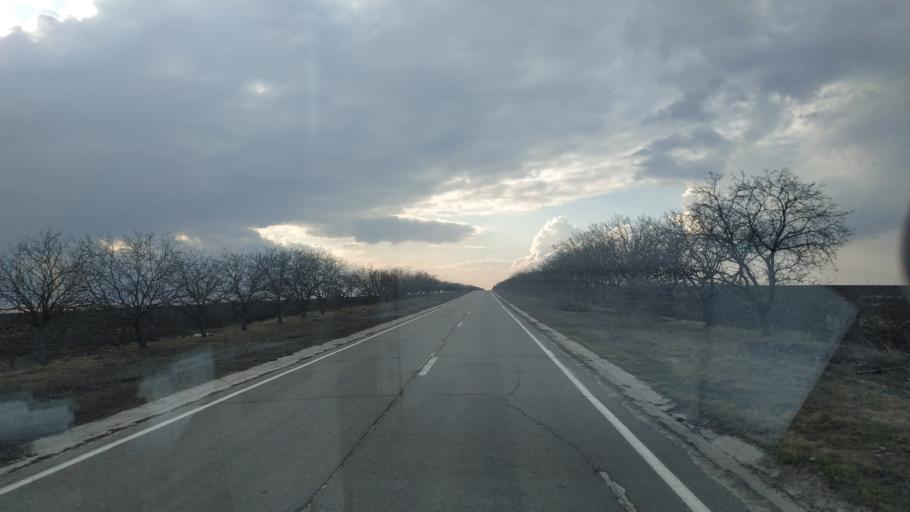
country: MD
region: Anenii Noi
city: Anenii Noi
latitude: 46.9224
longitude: 29.3370
